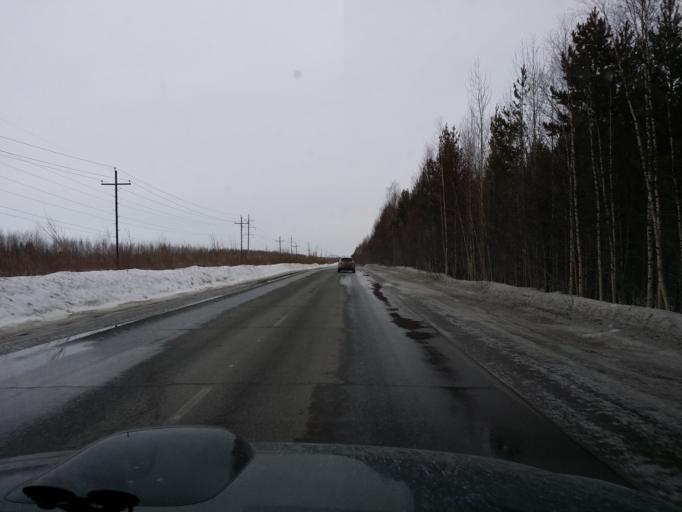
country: RU
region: Tomsk
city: Strezhevoy
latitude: 60.8026
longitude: 77.2908
